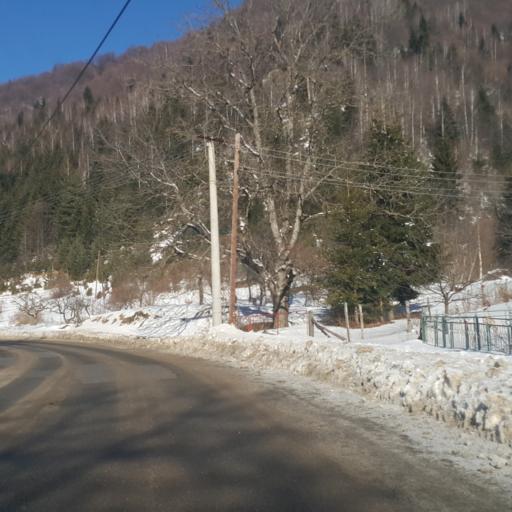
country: XK
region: Mitrovica
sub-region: Komuna e Leposaviqit
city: Leposaviq
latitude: 43.3051
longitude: 20.8746
